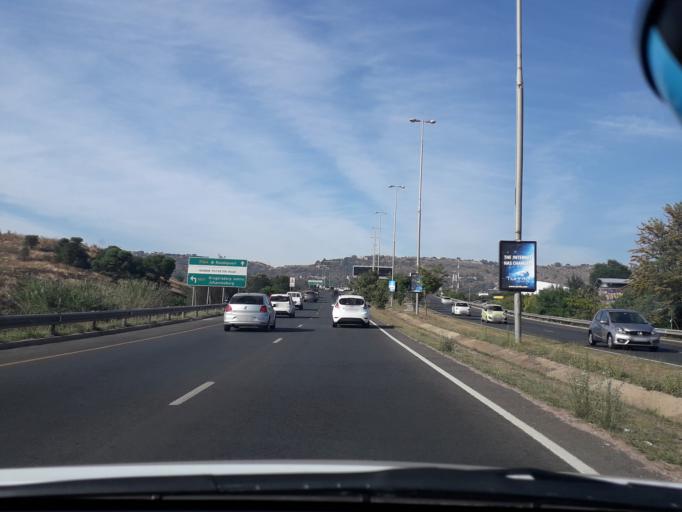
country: ZA
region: Gauteng
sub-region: City of Johannesburg Metropolitan Municipality
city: Roodepoort
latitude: -26.1221
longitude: 27.9119
